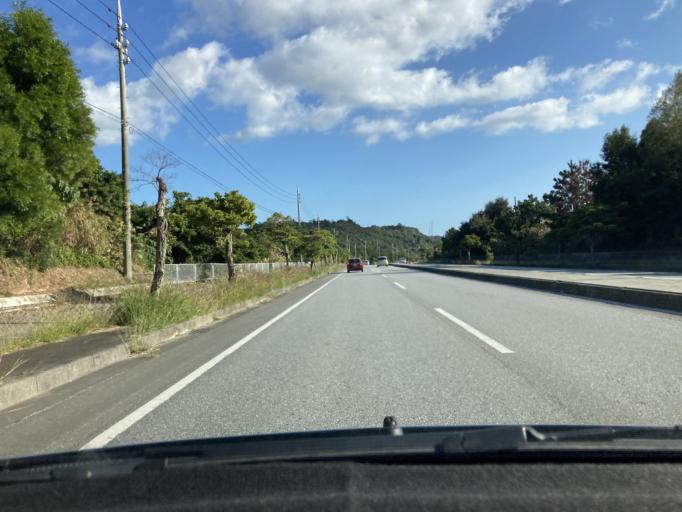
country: JP
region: Okinawa
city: Ishikawa
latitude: 26.4023
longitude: 127.8264
